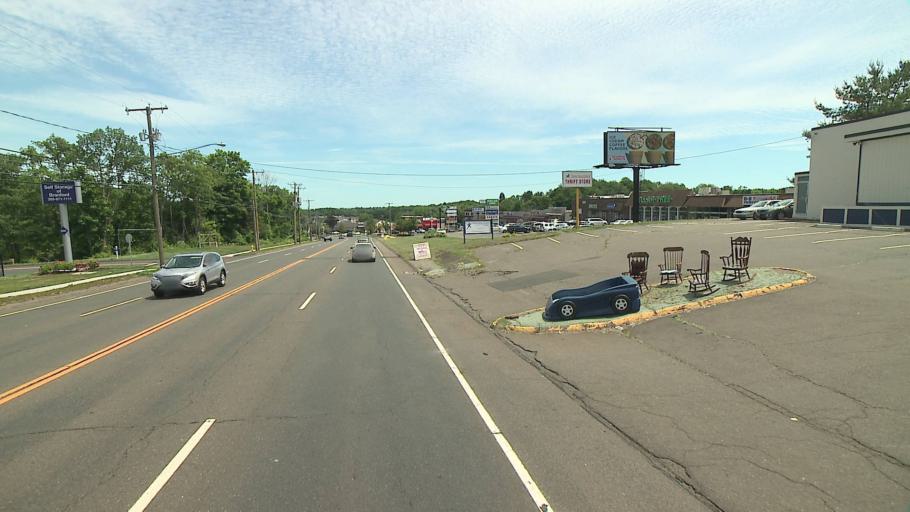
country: US
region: Connecticut
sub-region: New Haven County
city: Branford Center
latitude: 41.2776
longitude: -72.8392
